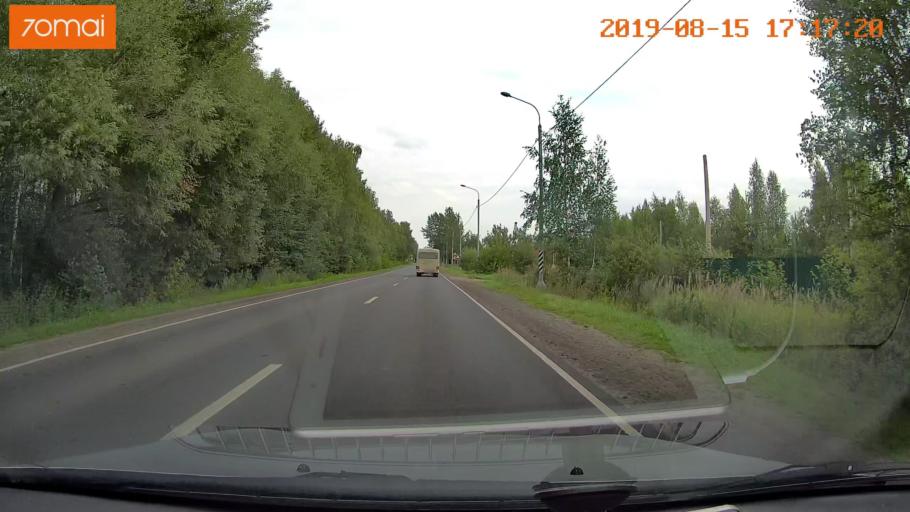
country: RU
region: Moskovskaya
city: Ashitkovo
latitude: 55.4355
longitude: 38.5230
